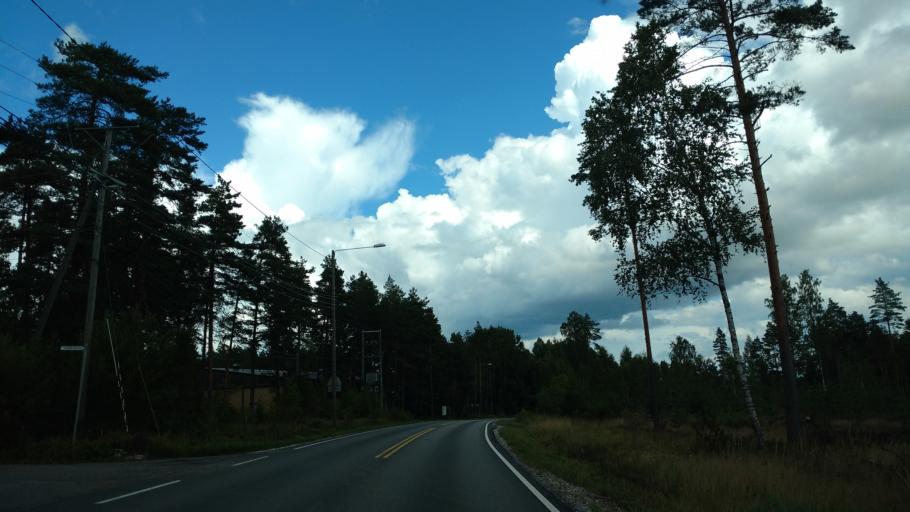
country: FI
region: Uusimaa
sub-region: Helsinki
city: Karjalohja
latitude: 60.2123
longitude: 23.6730
